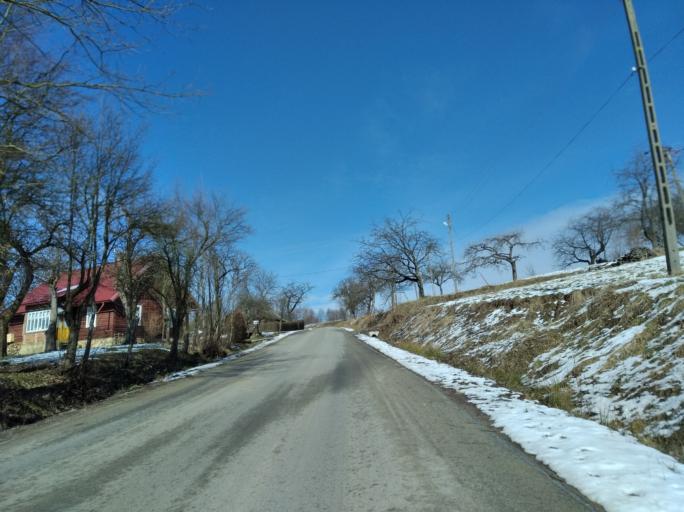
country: PL
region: Subcarpathian Voivodeship
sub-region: Powiat brzozowski
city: Jablonica Polska
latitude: 49.7224
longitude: 21.8797
